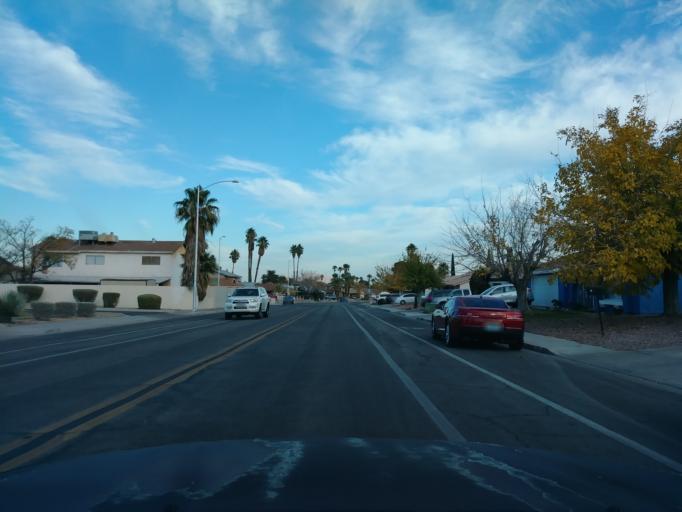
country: US
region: Nevada
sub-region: Clark County
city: Spring Valley
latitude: 36.1701
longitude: -115.2410
